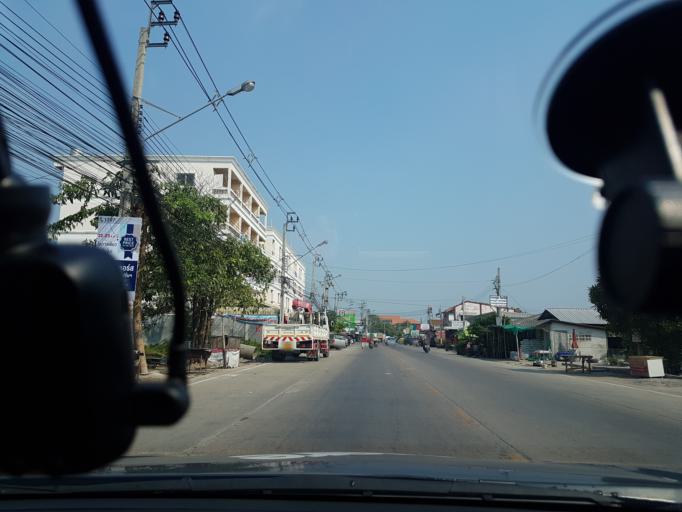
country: TH
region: Bangkok
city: Khlong Sam Wa
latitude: 13.8421
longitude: 100.7070
